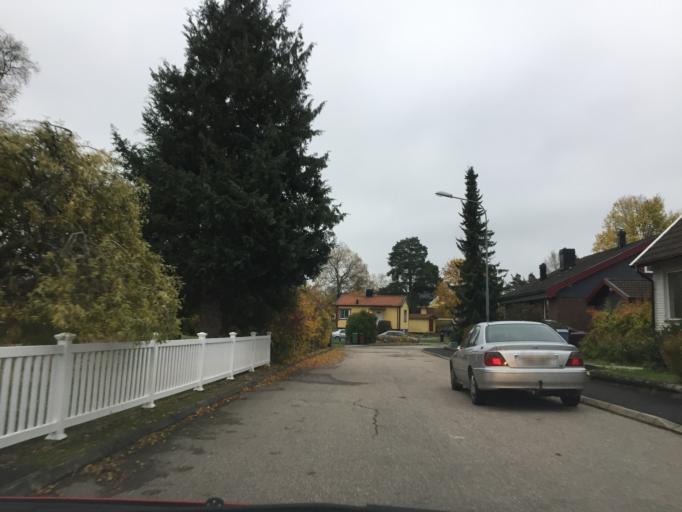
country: SE
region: Vaestra Goetaland
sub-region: Trollhattan
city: Trollhattan
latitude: 58.2573
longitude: 12.2880
